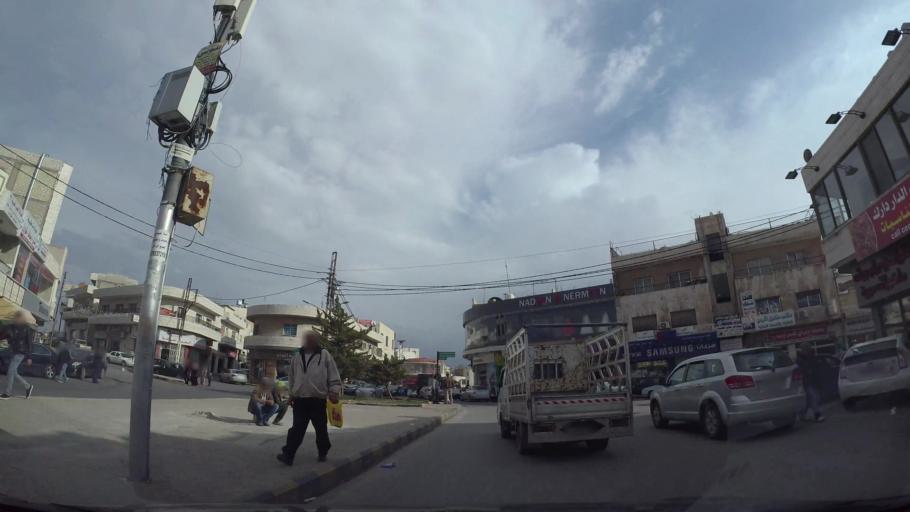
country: JO
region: Amman
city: Amman
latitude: 32.0000
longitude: 35.9439
